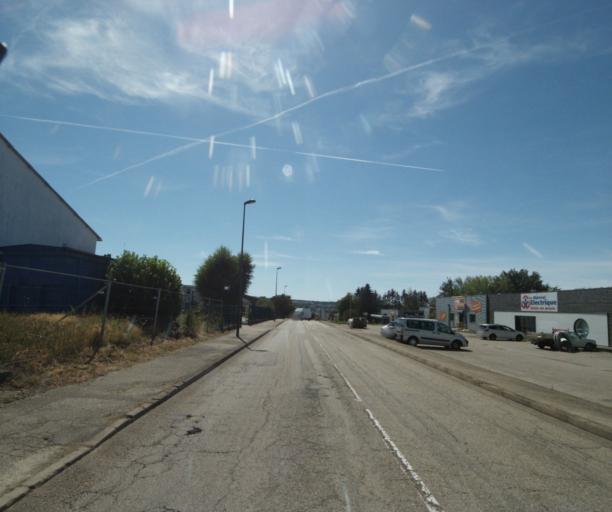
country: FR
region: Lorraine
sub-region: Departement des Vosges
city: Golbey
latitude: 48.2007
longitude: 6.4533
